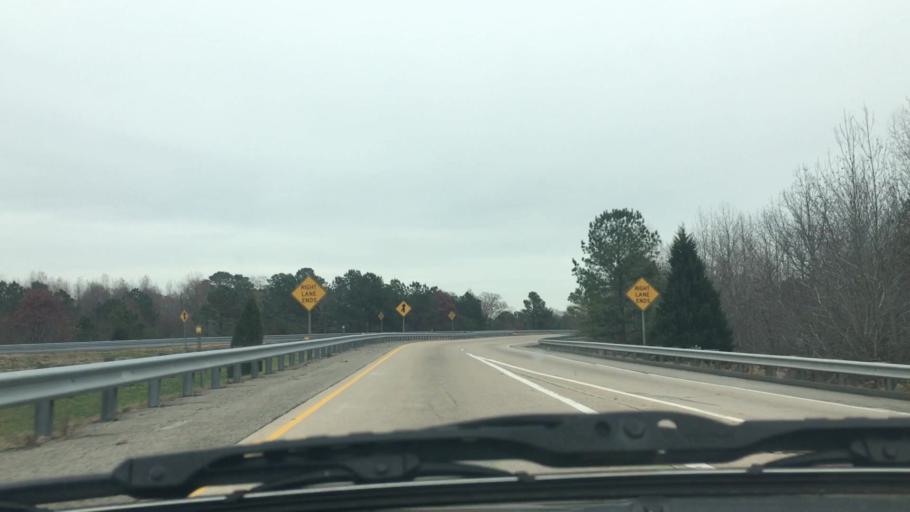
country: US
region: Virginia
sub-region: City of Portsmouth
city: Portsmouth Heights
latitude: 36.8665
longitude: -76.4288
